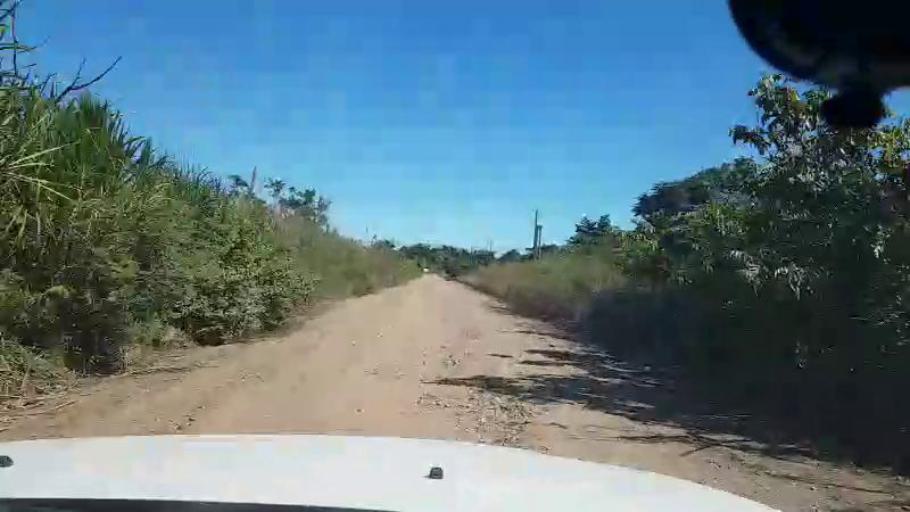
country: BZ
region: Stann Creek
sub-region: Dangriga
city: Dangriga
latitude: 17.1580
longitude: -88.3306
